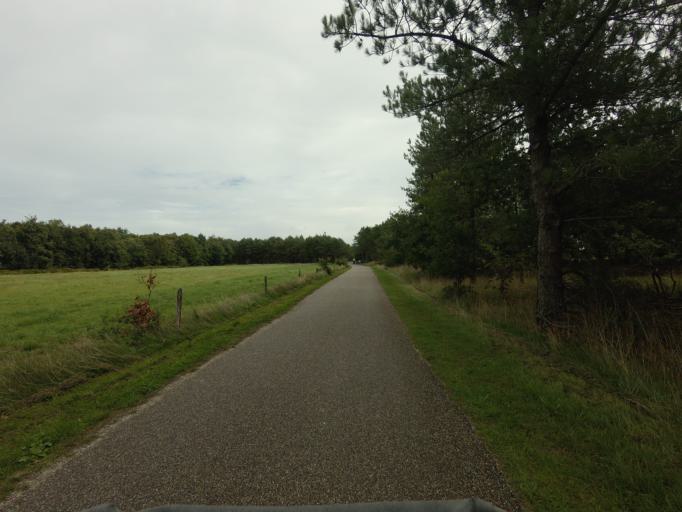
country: NL
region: Friesland
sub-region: Gemeente Ameland
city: Nes
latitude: 53.4523
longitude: 5.7835
